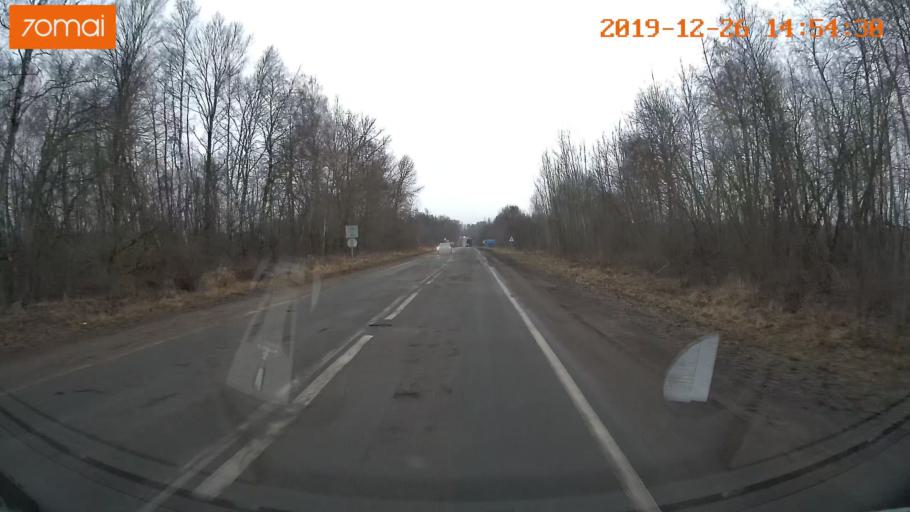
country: RU
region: Jaroslavl
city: Rybinsk
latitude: 58.3070
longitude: 38.8839
